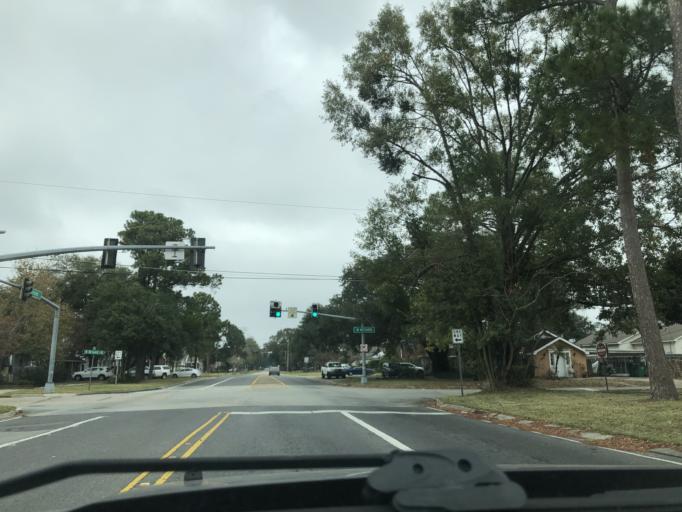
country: US
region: Louisiana
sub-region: Jefferson Parish
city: Metairie Terrace
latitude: 29.9819
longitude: -90.1603
